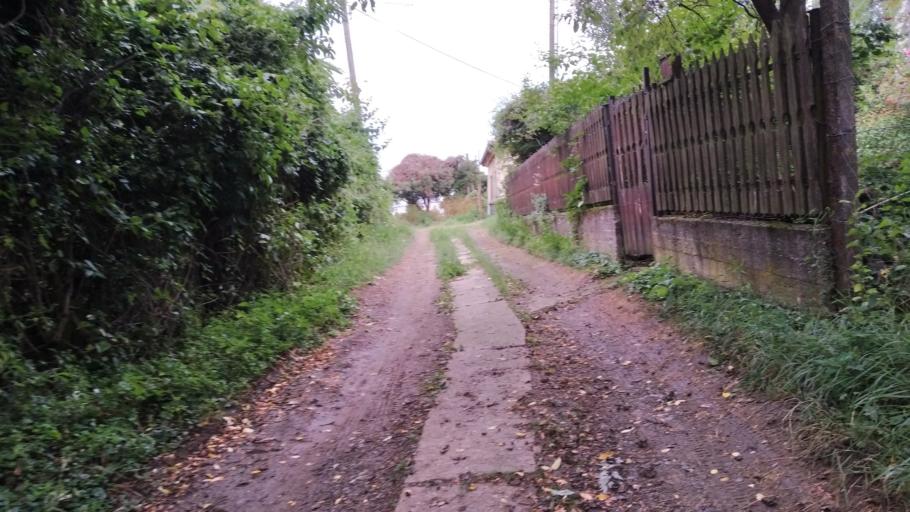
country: HU
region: Pest
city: Szob
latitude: 47.9337
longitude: 18.8268
